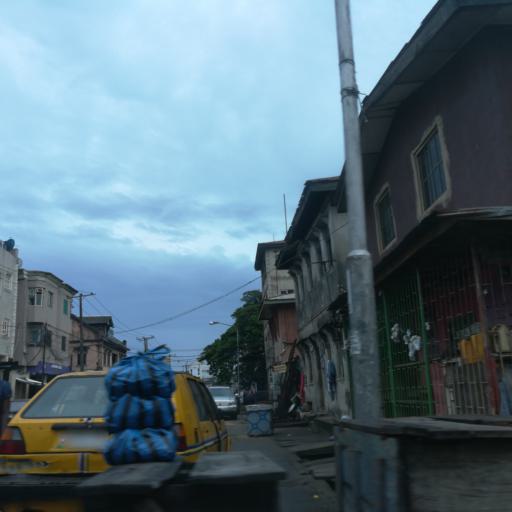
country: NG
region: Lagos
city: Ebute Metta
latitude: 6.4896
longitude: 3.3815
